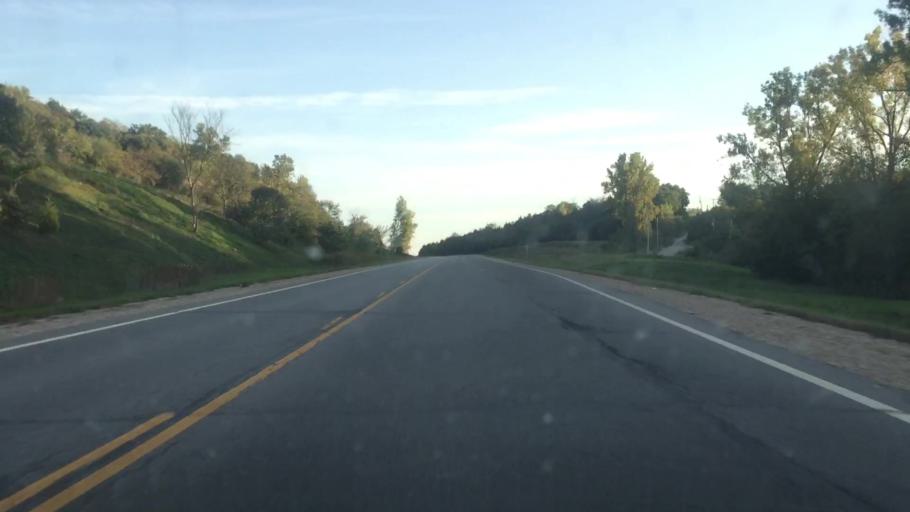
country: US
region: Kansas
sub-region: Atchison County
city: Atchison
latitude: 39.4945
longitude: -95.1319
